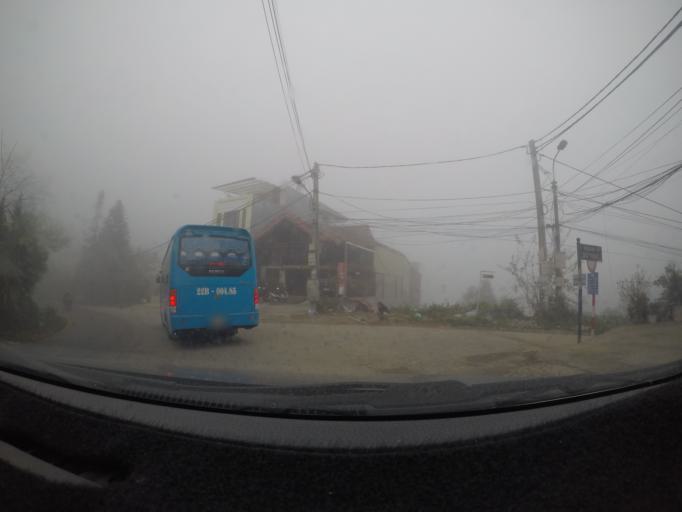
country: VN
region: Lao Cai
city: Sa Pa
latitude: 22.3397
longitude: 103.8407
